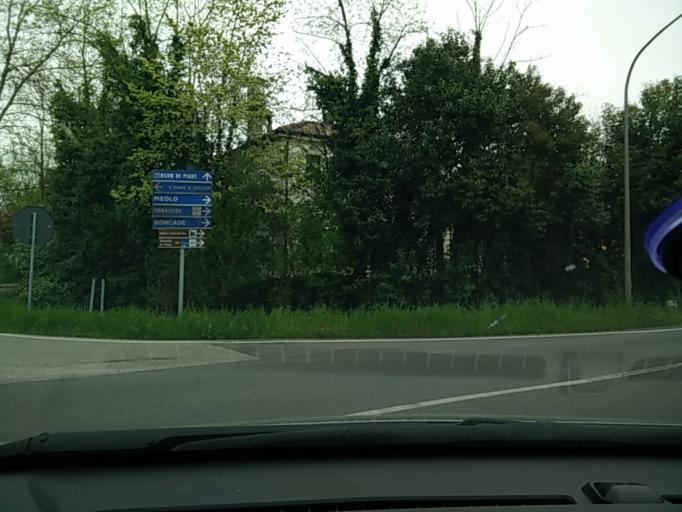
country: IT
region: Veneto
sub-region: Provincia di Treviso
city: Monastier di Treviso
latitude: 45.6594
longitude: 12.4175
